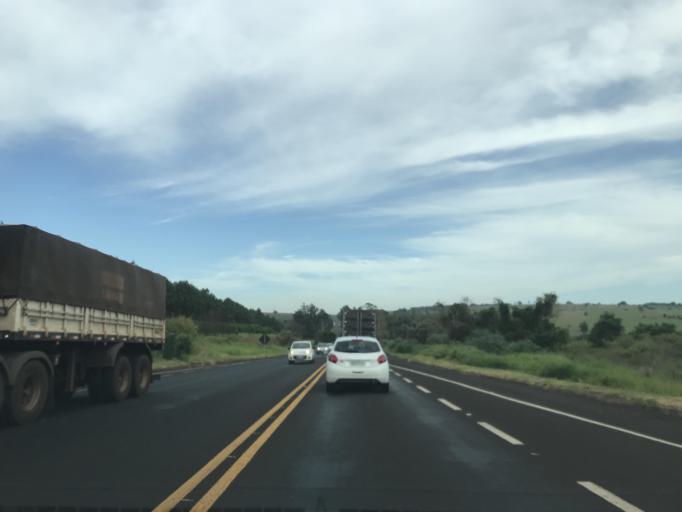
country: BR
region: Parana
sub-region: Paranavai
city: Paranavai
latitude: -23.0004
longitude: -52.5641
